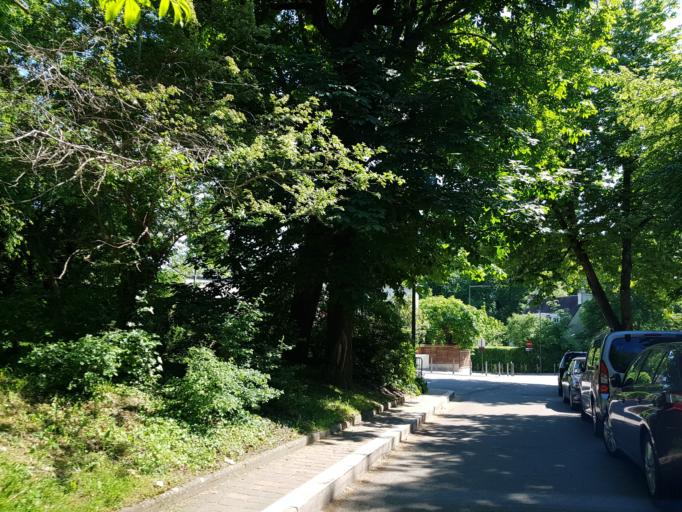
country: FR
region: Ile-de-France
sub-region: Departement des Hauts-de-Seine
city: Chatenay-Malabry
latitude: 48.7753
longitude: 2.2691
